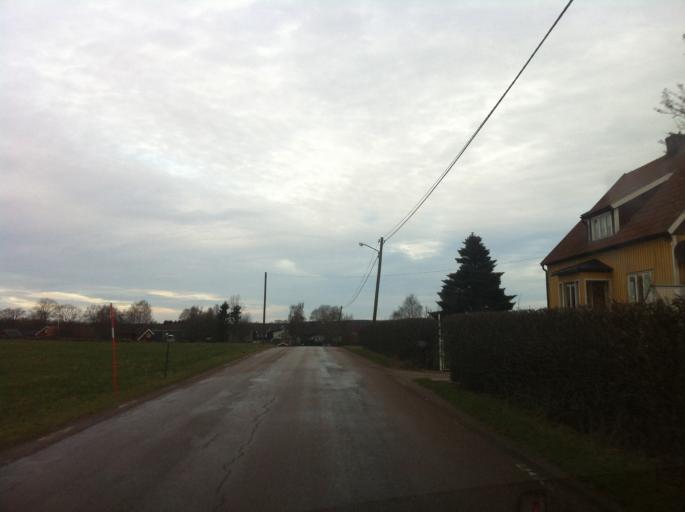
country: SE
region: Skane
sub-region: Svalovs Kommun
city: Kagerod
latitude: 56.0435
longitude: 13.1029
